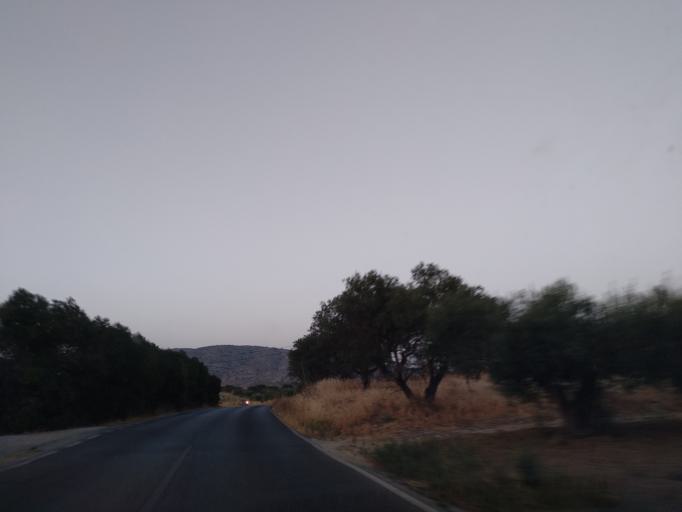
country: ES
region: Andalusia
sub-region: Provincia de Malaga
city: Cartama
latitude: 36.6776
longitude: -4.6593
